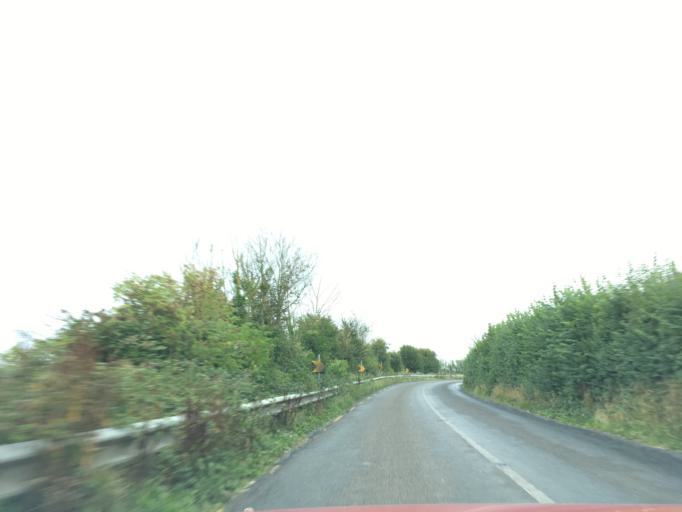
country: IE
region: Munster
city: Cashel
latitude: 52.4524
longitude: -7.8146
